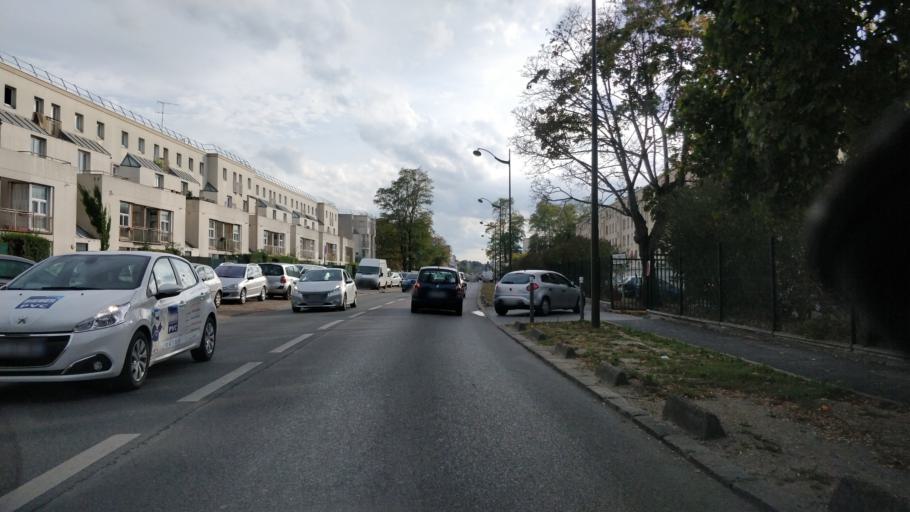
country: FR
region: Ile-de-France
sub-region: Departement de Seine-Saint-Denis
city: Clichy-sous-Bois
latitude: 48.9082
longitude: 2.5501
